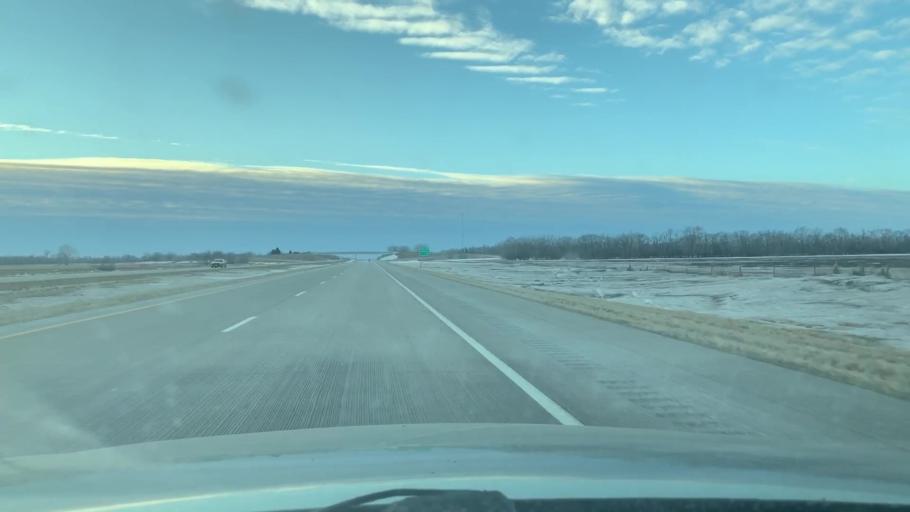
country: US
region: North Dakota
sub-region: Cass County
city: Casselton
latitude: 46.8751
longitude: -97.4214
